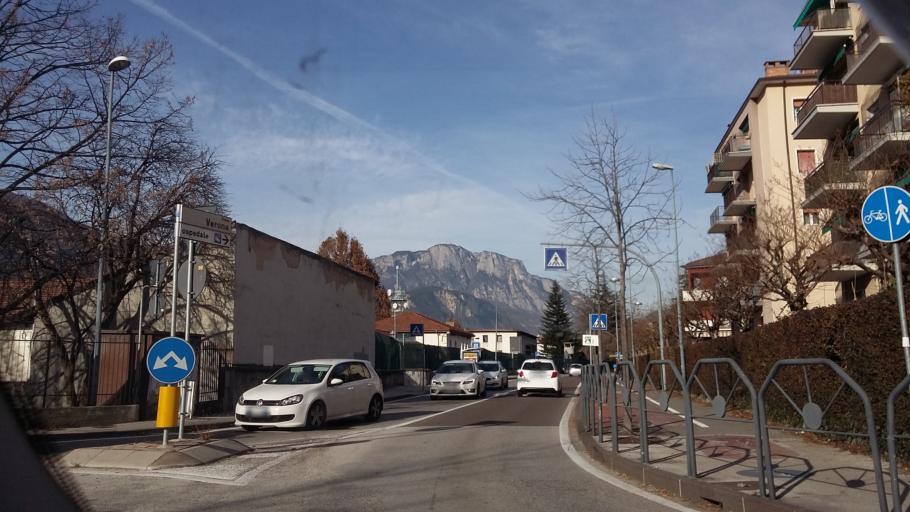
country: IT
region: Trentino-Alto Adige
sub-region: Provincia di Trento
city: Trento
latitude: 46.0501
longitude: 11.1311
